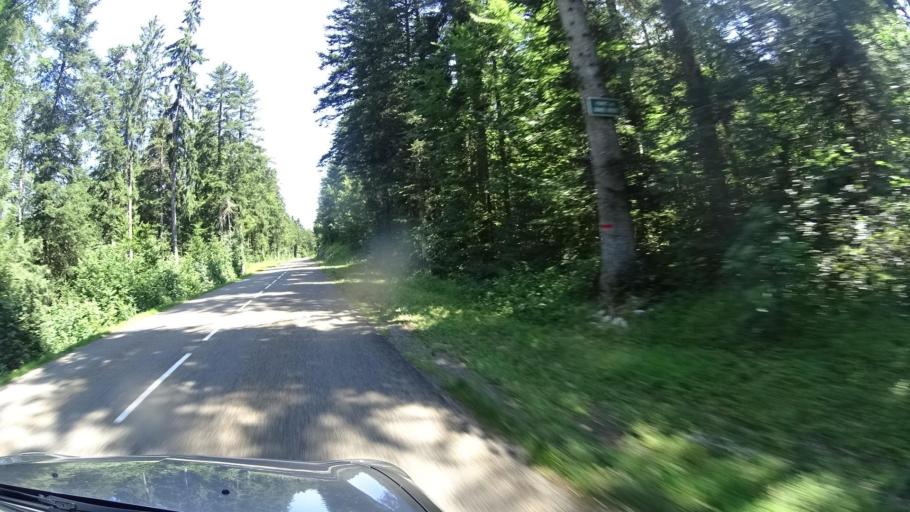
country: FR
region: Franche-Comte
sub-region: Departement du Jura
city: Longchaumois
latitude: 46.5114
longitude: 5.8948
